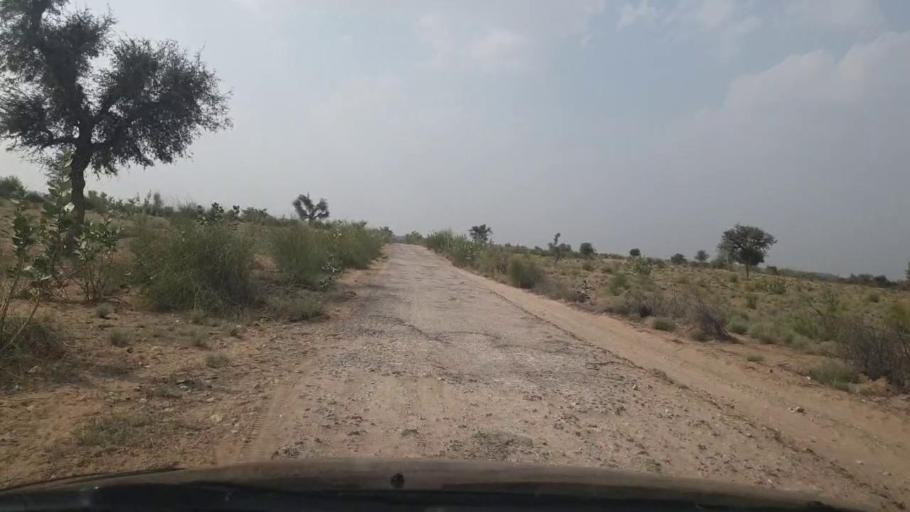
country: PK
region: Sindh
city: Islamkot
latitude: 24.9631
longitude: 70.6284
